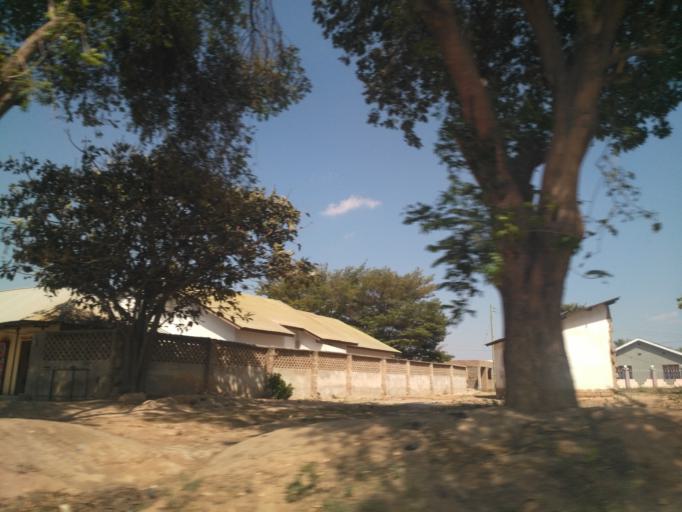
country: TZ
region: Dodoma
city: Dodoma
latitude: -6.1596
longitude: 35.7212
